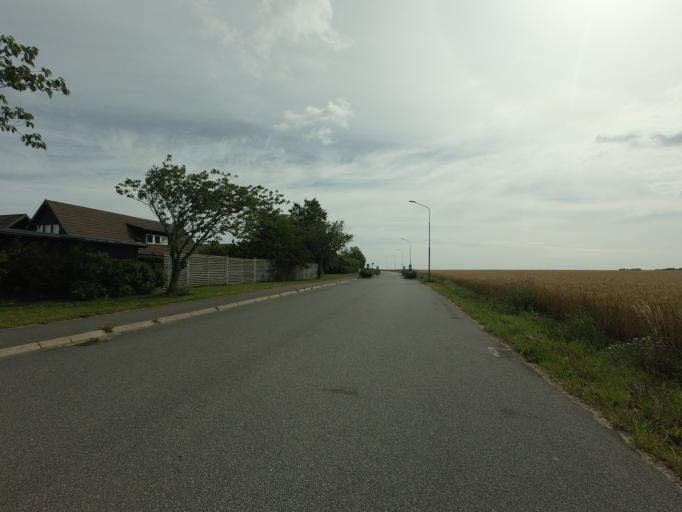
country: SE
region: Skane
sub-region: Simrishamns Kommun
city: Simrishamn
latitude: 55.5398
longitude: 14.3425
